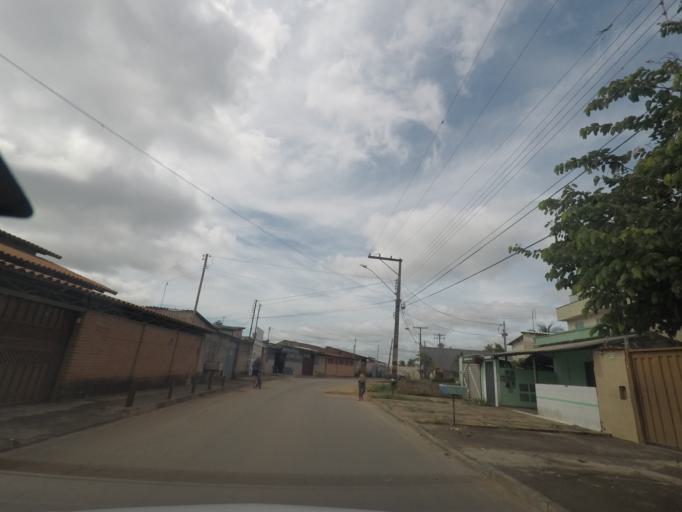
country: BR
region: Goias
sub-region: Goiania
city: Goiania
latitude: -16.6691
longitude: -49.1844
